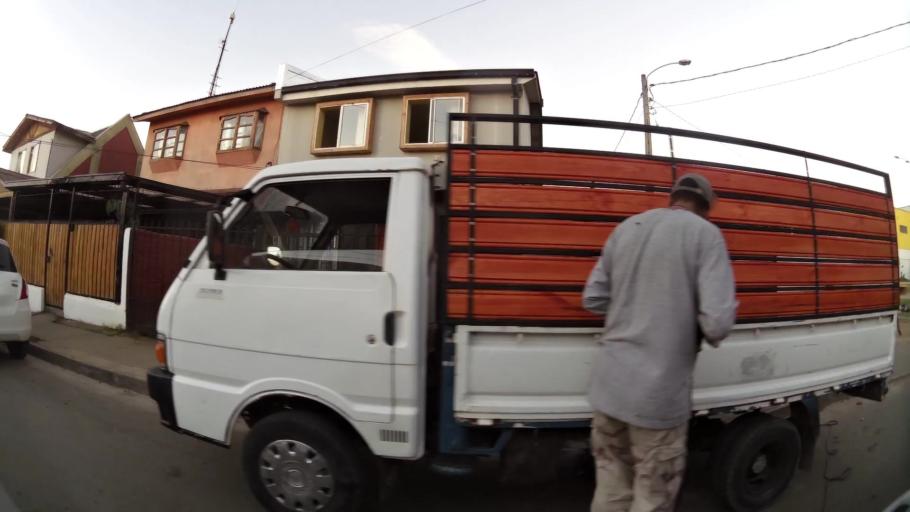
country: CL
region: Maule
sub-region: Provincia de Talca
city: Talca
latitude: -35.4490
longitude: -71.6257
